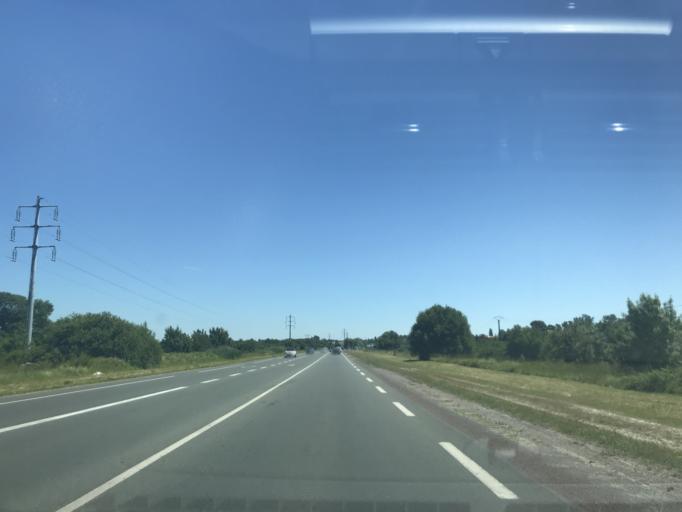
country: FR
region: Poitou-Charentes
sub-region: Departement de la Charente-Maritime
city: Saint-Georges-de-Didonne
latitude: 45.6205
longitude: -0.9938
